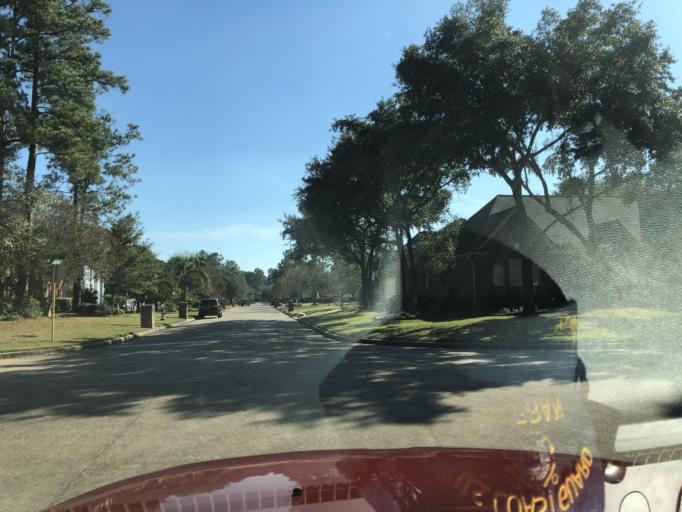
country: US
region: Texas
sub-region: Harris County
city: Tomball
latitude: 30.0328
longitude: -95.5442
